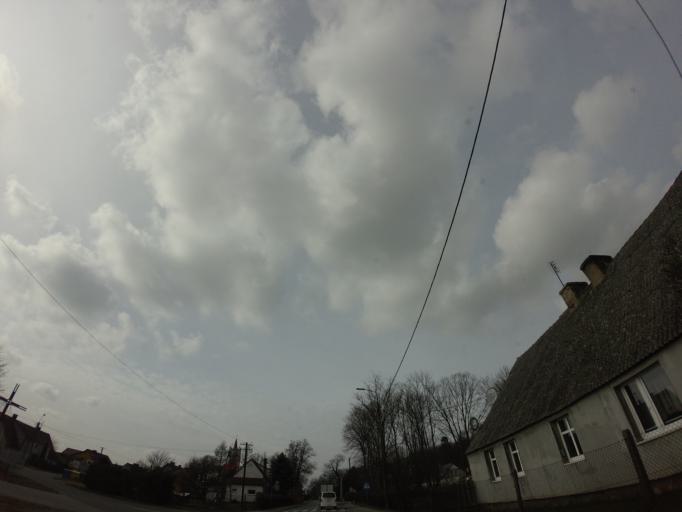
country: PL
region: West Pomeranian Voivodeship
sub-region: Powiat walecki
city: Walcz
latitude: 53.3139
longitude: 16.3509
